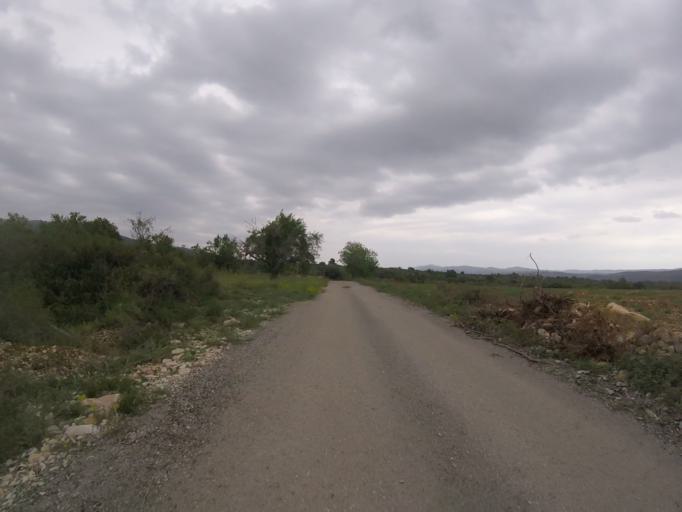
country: ES
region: Valencia
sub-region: Provincia de Castello
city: Cuevas de Vinroma
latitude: 40.2909
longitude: 0.0862
